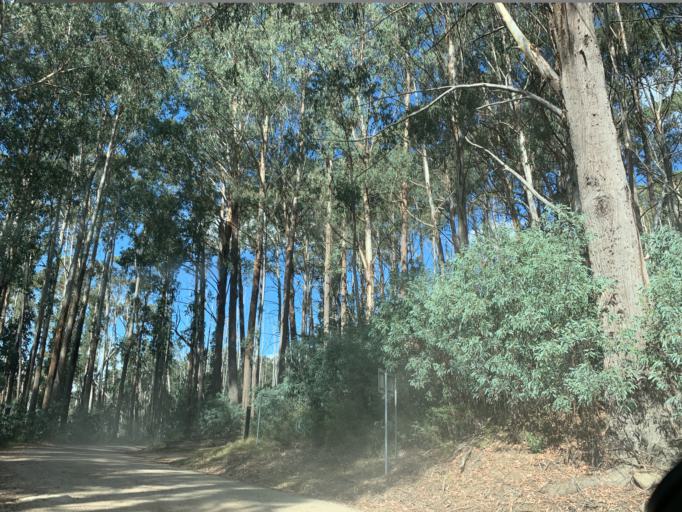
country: AU
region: Victoria
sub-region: Mansfield
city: Mansfield
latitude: -37.0998
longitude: 146.4655
